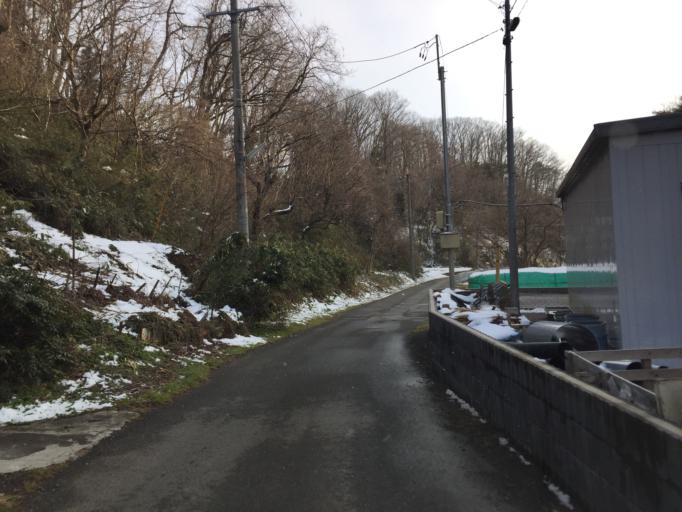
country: JP
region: Fukushima
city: Fukushima-shi
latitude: 37.8358
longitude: 140.4584
